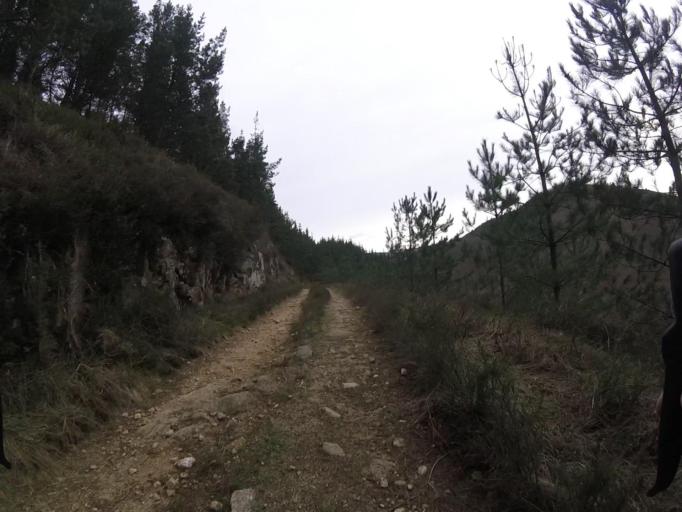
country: ES
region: Navarre
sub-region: Provincia de Navarra
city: Bera
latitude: 43.2911
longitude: -1.7340
